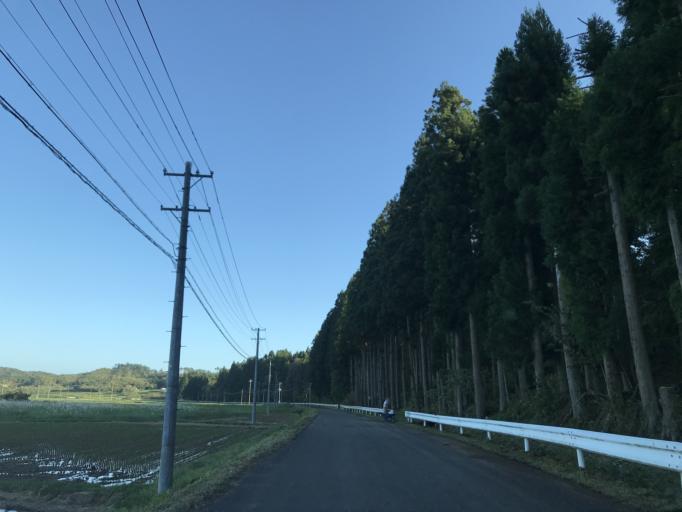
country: JP
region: Iwate
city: Ichinoseki
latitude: 38.9408
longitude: 141.0487
